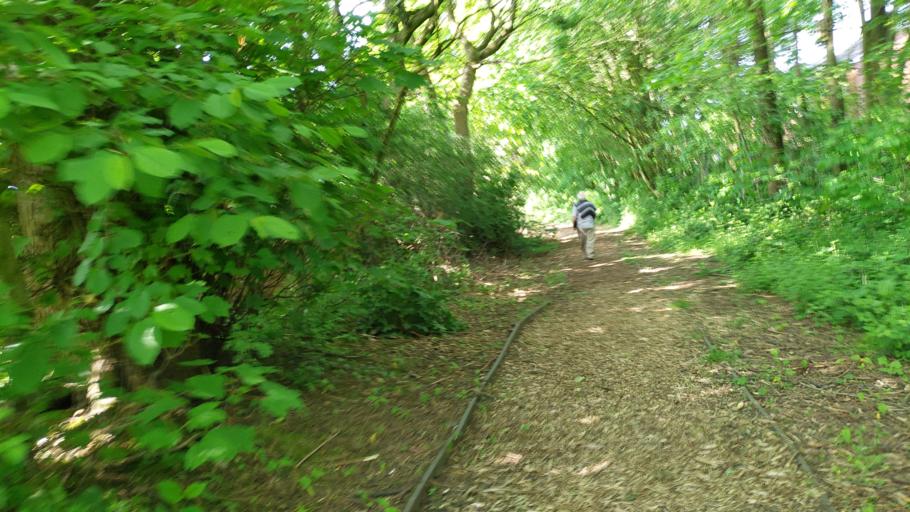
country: GB
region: England
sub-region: Lancashire
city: Chorley
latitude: 53.6647
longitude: -2.6390
